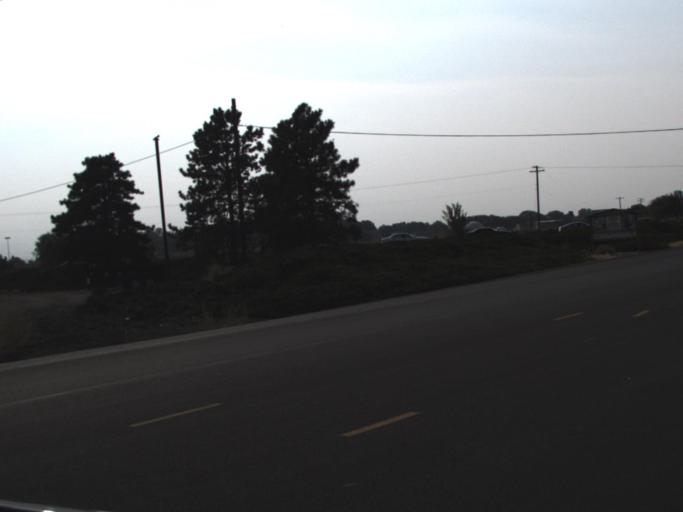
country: US
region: Washington
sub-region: Yakima County
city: Toppenish
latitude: 46.3698
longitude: -120.3190
